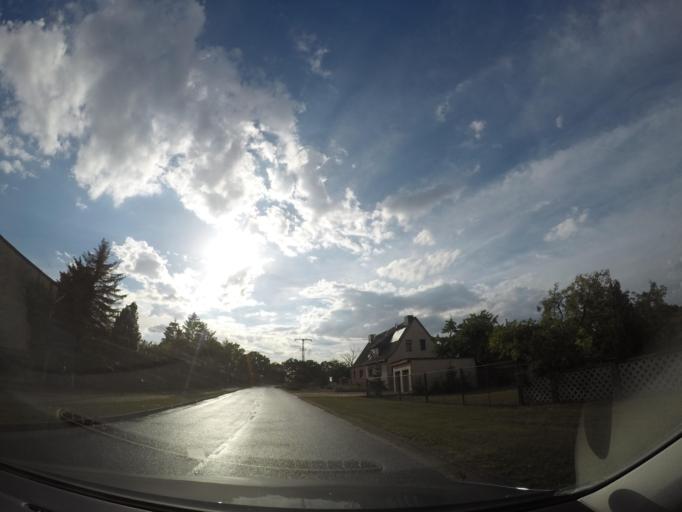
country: DE
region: Saxony-Anhalt
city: Mieste
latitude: 52.5106
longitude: 11.1792
